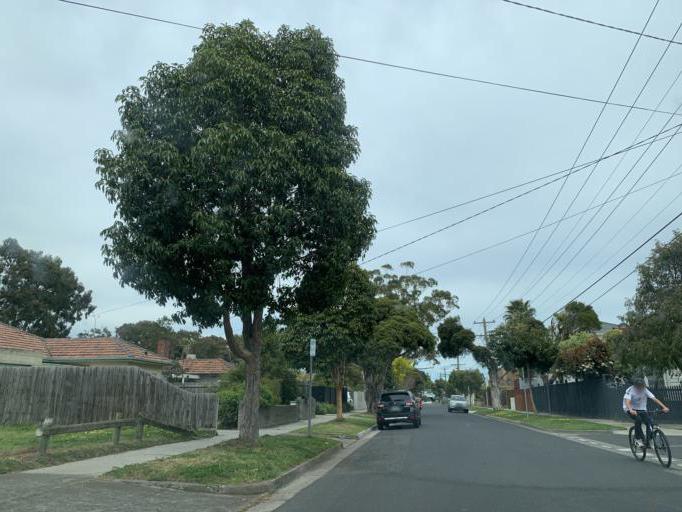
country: AU
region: Victoria
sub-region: Bayside
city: Highett
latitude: -37.9532
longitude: 145.0389
